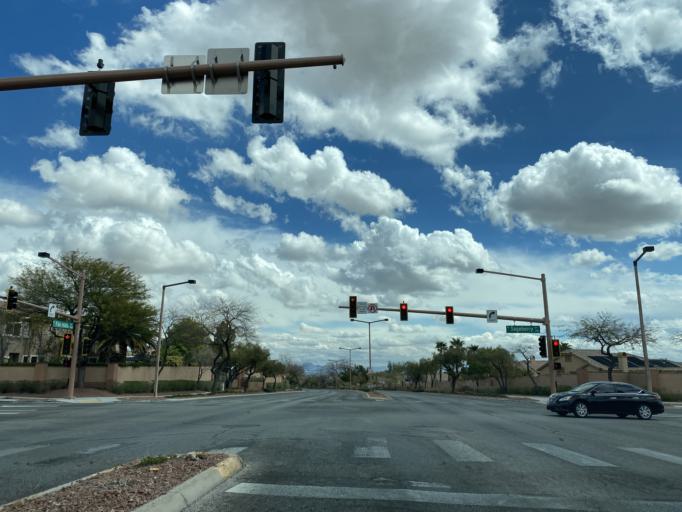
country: US
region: Nevada
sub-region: Clark County
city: Summerlin South
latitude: 36.1824
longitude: -115.3383
